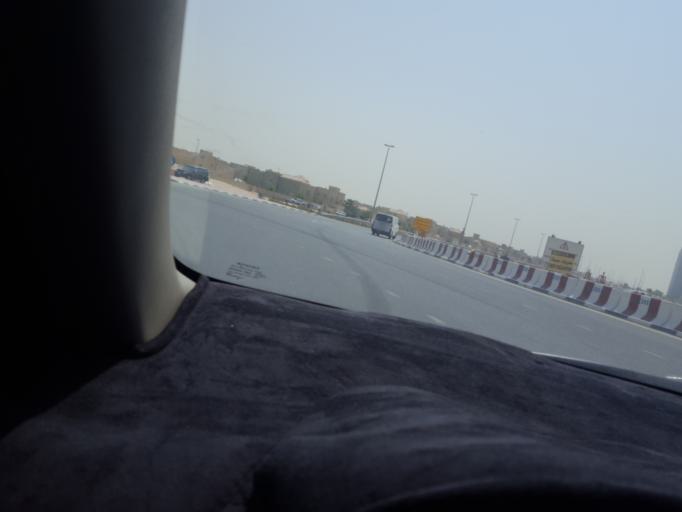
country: AE
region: Dubai
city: Dubai
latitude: 25.0803
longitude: 55.2316
